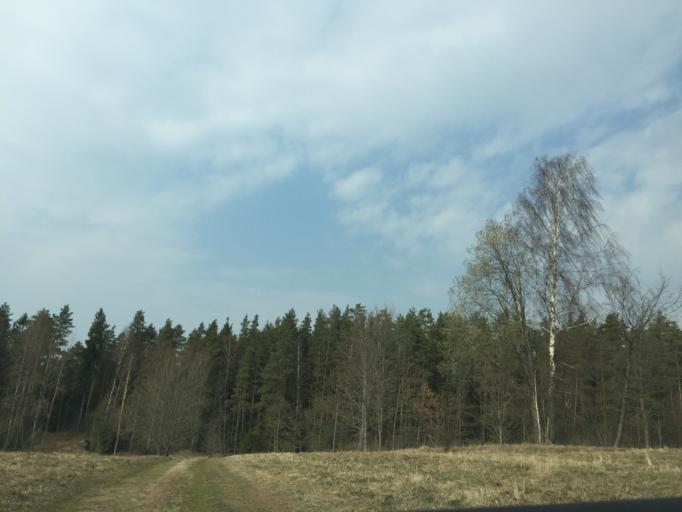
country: LV
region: Amatas Novads
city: Drabesi
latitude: 57.2288
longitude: 25.1937
